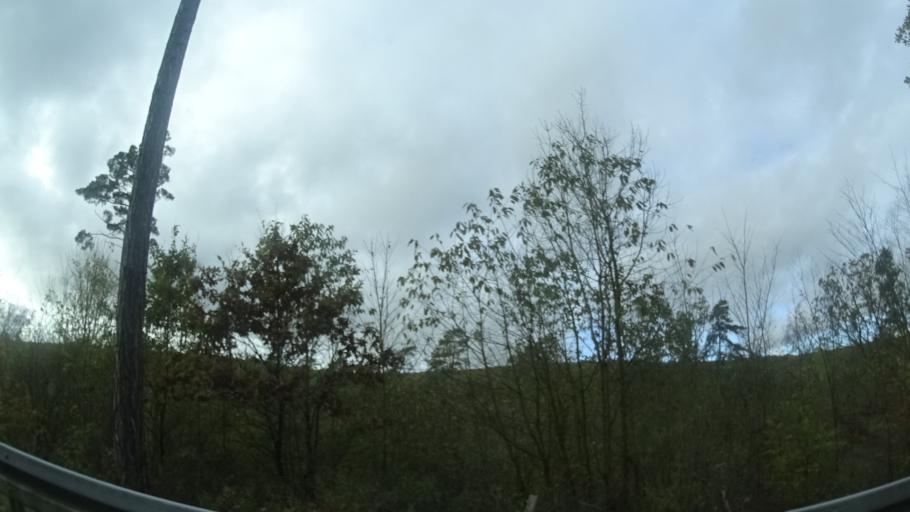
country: DE
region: Bavaria
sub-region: Regierungsbezirk Unterfranken
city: Aubstadt
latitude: 50.3540
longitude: 10.4191
